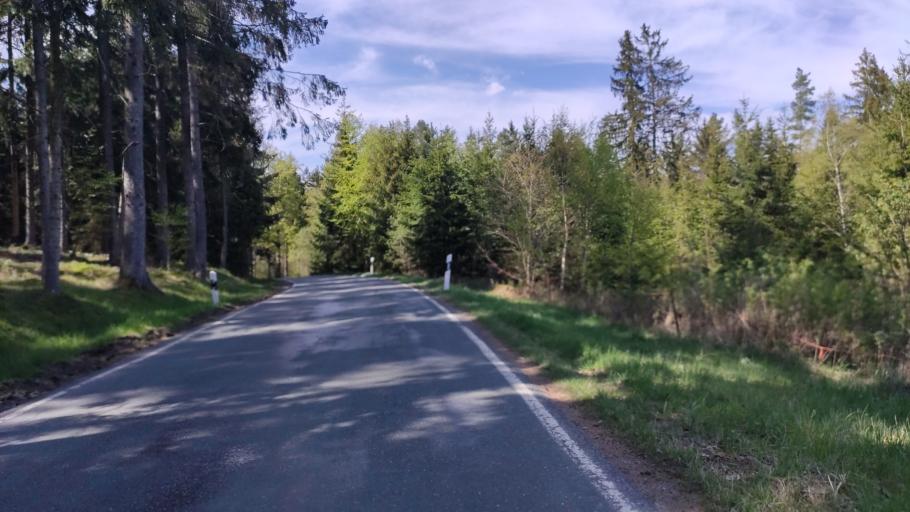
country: DE
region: Thuringia
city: Leutenberg
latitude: 50.5026
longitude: 11.4578
